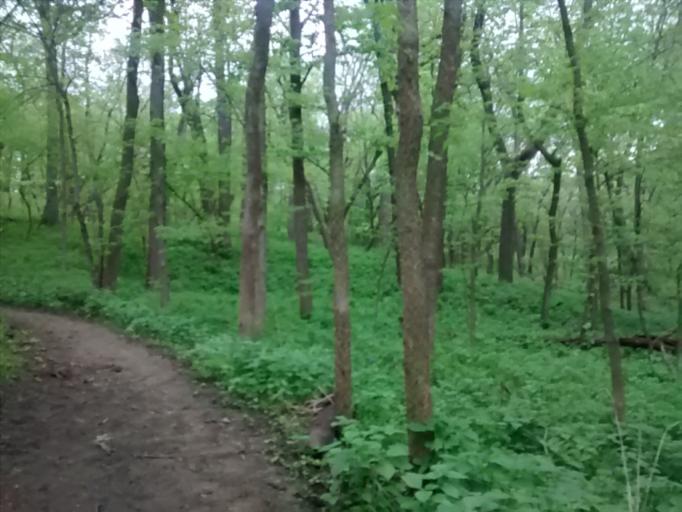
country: US
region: Nebraska
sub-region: Sarpy County
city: Bellevue
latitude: 41.1784
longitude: -95.9100
